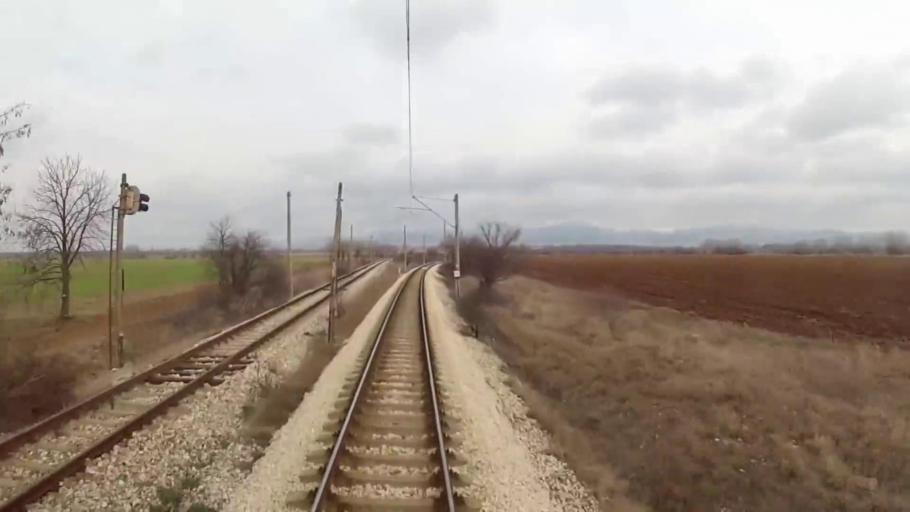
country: BG
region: Sofiya
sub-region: Obshtina Elin Pelin
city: Elin Pelin
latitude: 42.7134
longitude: 23.5769
